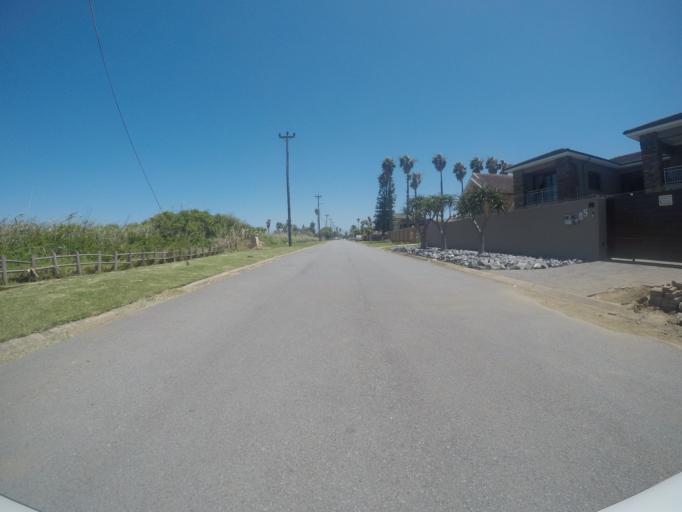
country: ZA
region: Eastern Cape
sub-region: Buffalo City Metropolitan Municipality
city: East London
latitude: -32.9511
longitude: 28.0122
